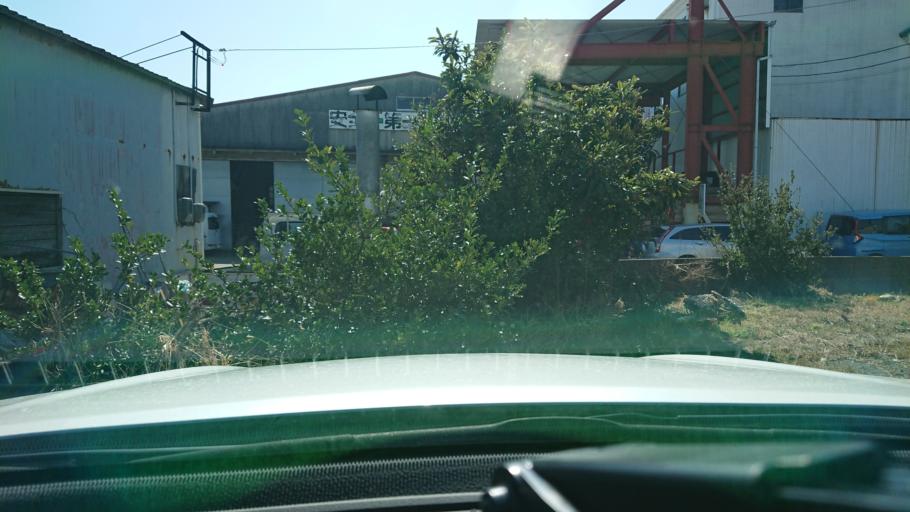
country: JP
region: Tokushima
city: Narutocho-mitsuishi
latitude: 34.1535
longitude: 134.5933
